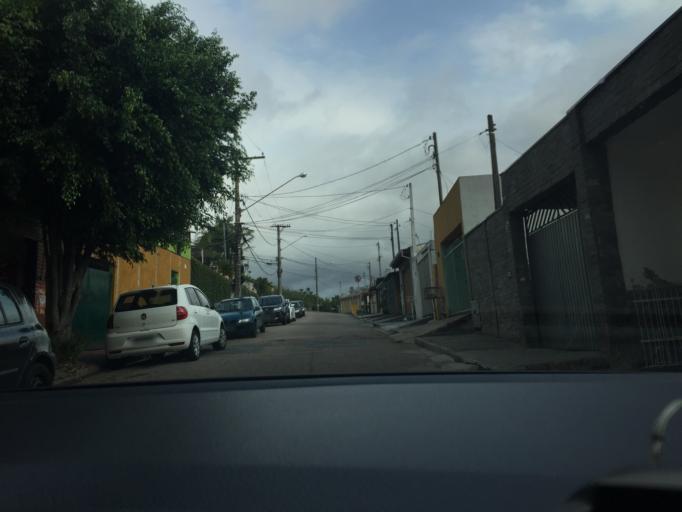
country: BR
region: Sao Paulo
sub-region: Jundiai
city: Jundiai
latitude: -23.2047
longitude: -46.8982
